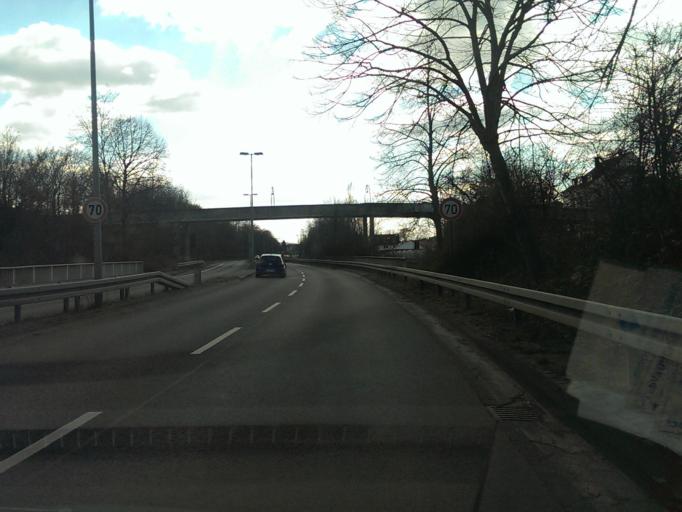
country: DE
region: Lower Saxony
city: Hildesheim
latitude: 52.1503
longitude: 9.9660
